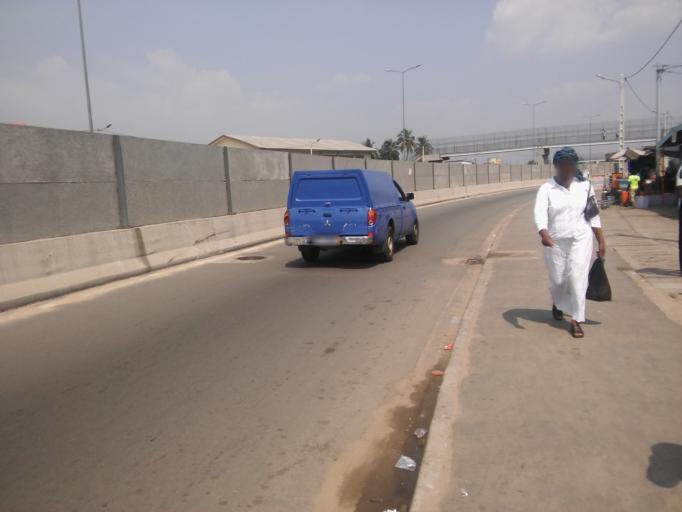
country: CI
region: Lagunes
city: Abidjan
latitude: 5.2982
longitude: -3.9802
